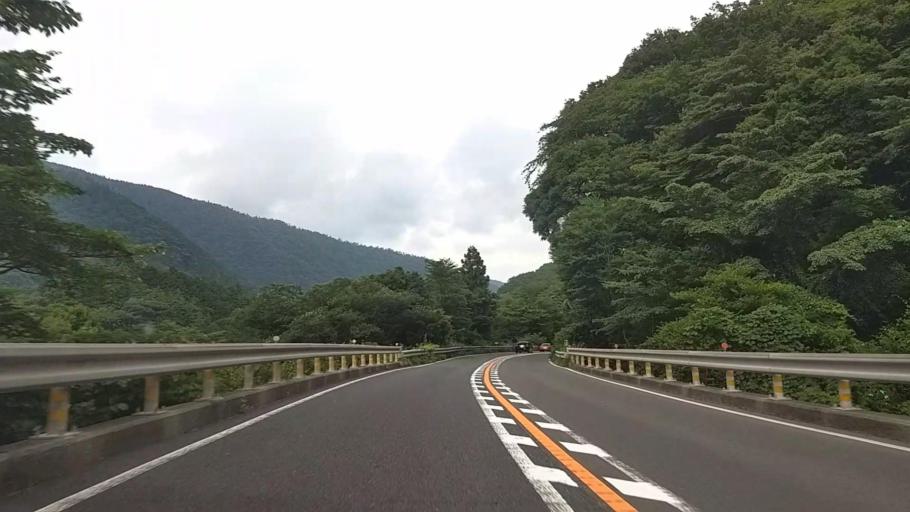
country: JP
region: Kanagawa
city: Hakone
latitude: 35.2116
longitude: 139.0646
